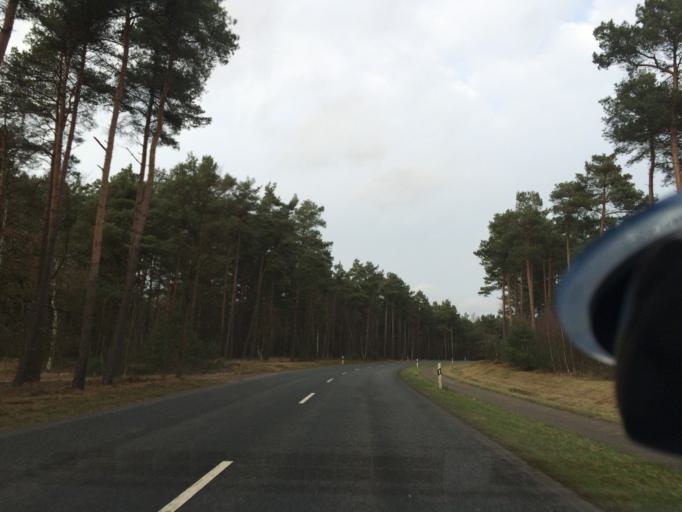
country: DE
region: Lower Saxony
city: Soltau
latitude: 52.9915
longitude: 9.9206
